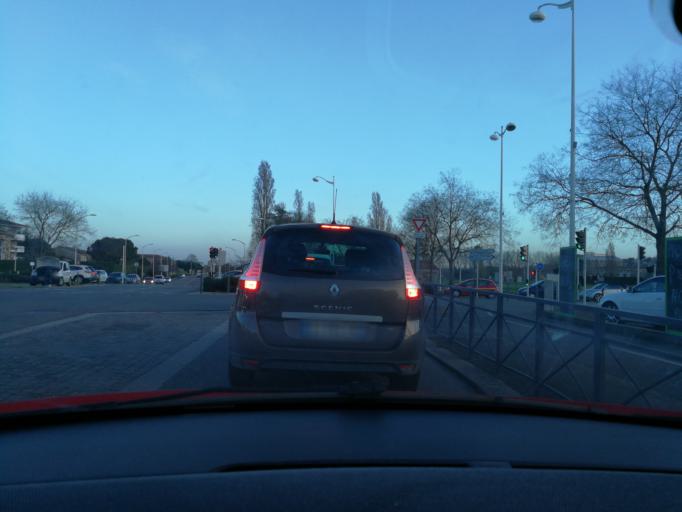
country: FR
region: Midi-Pyrenees
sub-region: Departement de la Haute-Garonne
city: Balma
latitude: 43.6095
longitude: 1.4901
